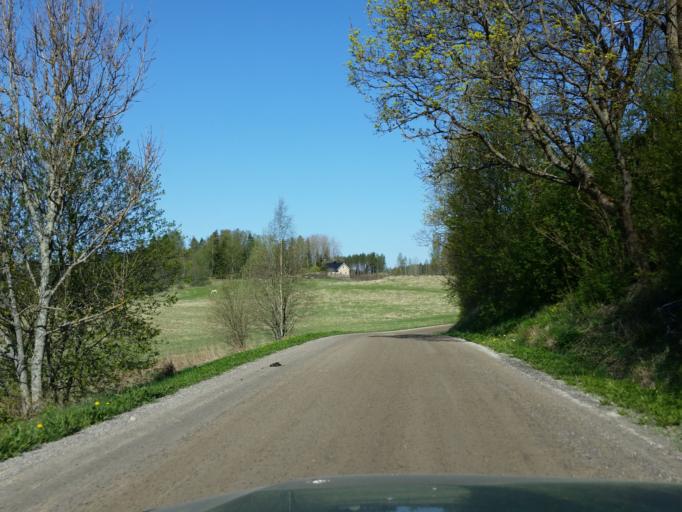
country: FI
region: Uusimaa
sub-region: Helsinki
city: Karjalohja
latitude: 60.1410
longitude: 23.7375
